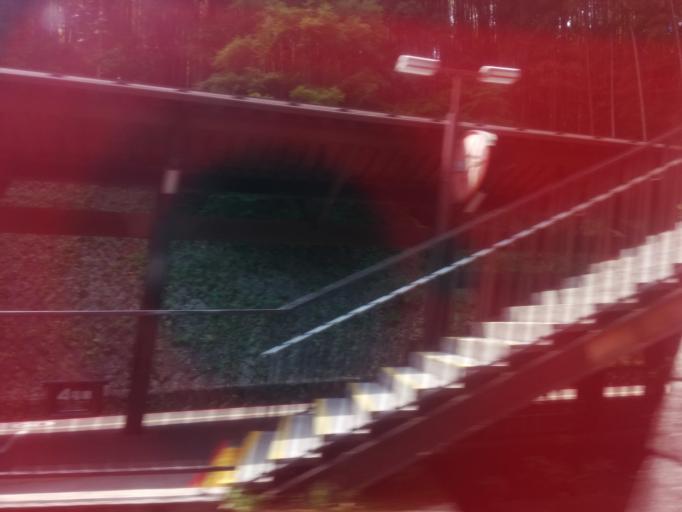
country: JP
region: Kyoto
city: Muko
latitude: 35.0171
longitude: 135.6704
